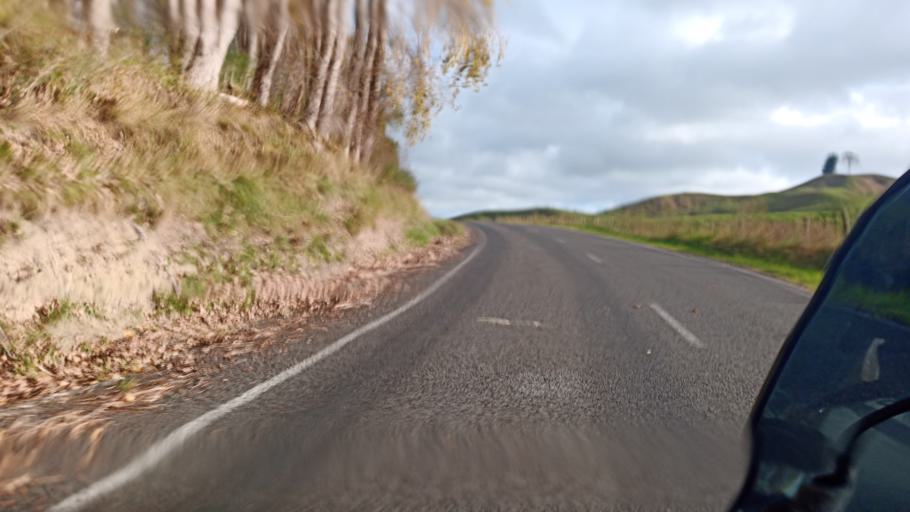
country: NZ
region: Gisborne
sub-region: Gisborne District
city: Gisborne
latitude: -38.5532
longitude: 177.6960
